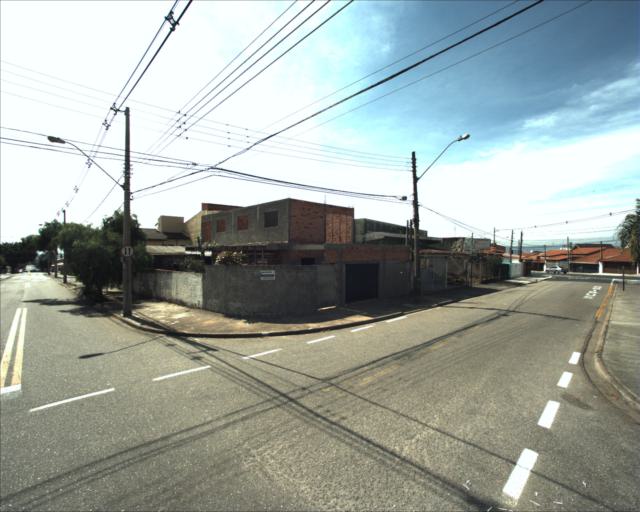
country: BR
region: Sao Paulo
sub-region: Sorocaba
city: Sorocaba
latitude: -23.5187
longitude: -47.5097
